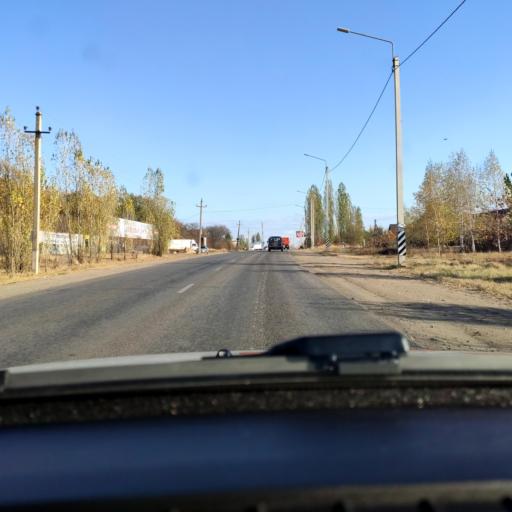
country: RU
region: Voronezj
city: Semiluki
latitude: 51.7271
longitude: 39.0306
